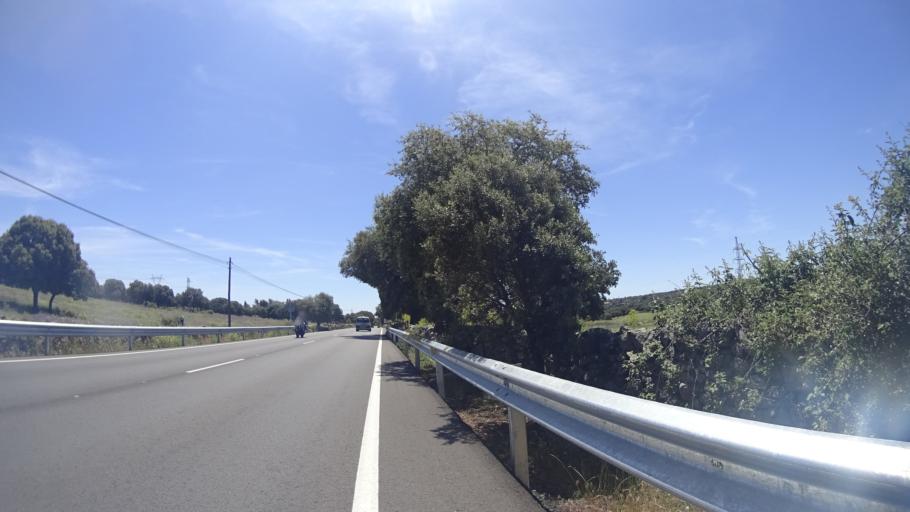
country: ES
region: Madrid
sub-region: Provincia de Madrid
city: Galapagar
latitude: 40.5960
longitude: -4.0155
